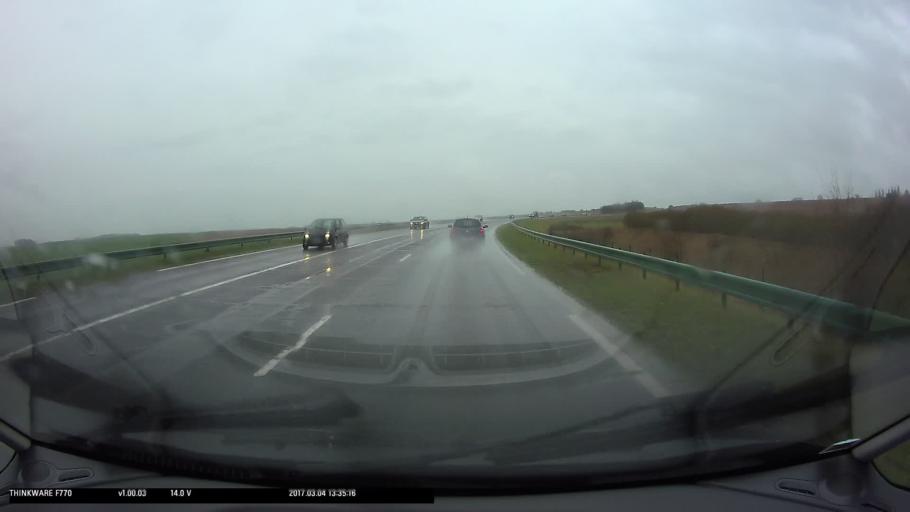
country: FR
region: Ile-de-France
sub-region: Departement du Val-d'Oise
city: Marines
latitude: 49.1195
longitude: 2.0285
